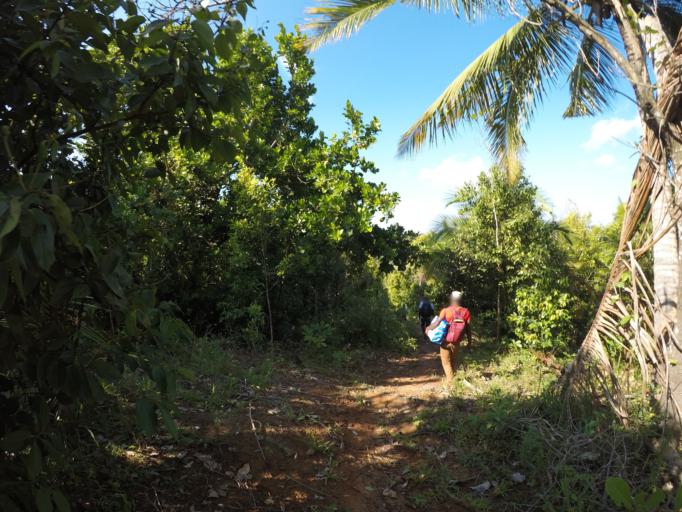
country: TZ
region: Pemba South
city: Mtambile
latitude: -5.3866
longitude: 39.7261
